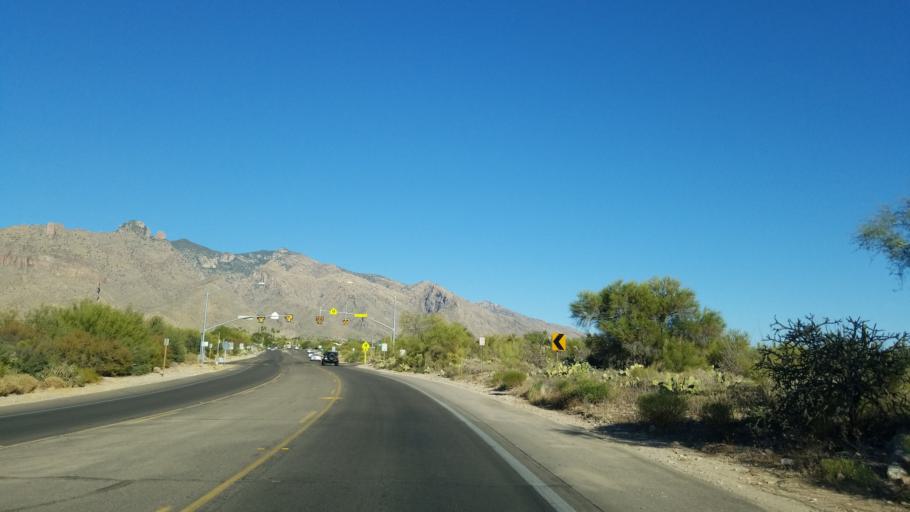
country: US
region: Arizona
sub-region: Pima County
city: Catalina Foothills
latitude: 32.3236
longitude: -110.9415
